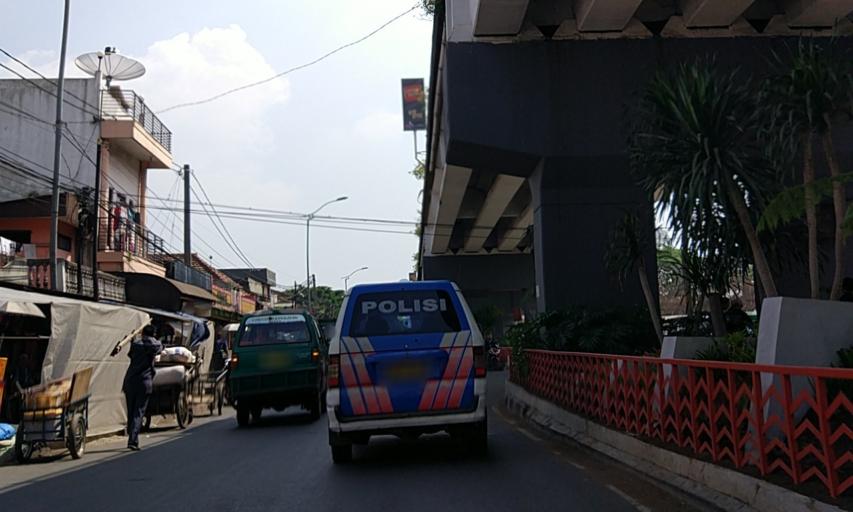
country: ID
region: West Java
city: Cimahi
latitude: -6.8961
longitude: 107.5603
